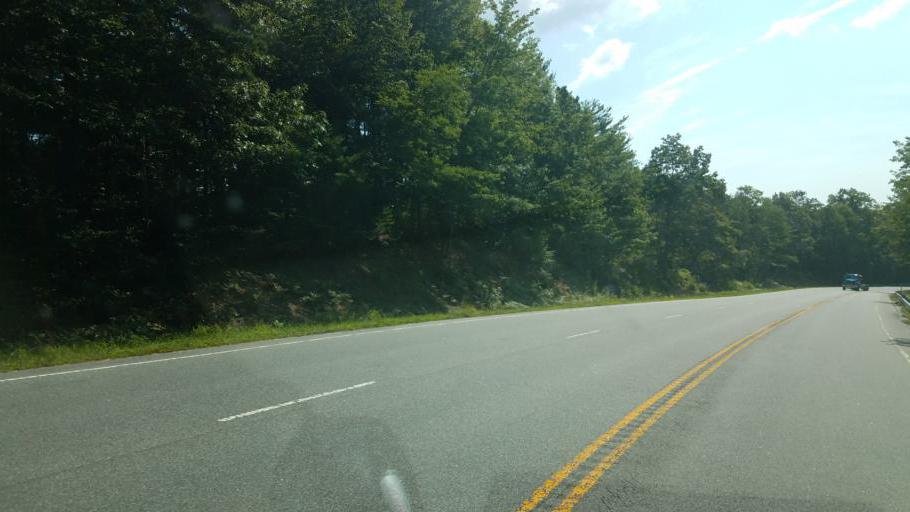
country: US
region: North Carolina
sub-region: Avery County
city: Newland
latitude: 35.9353
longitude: -81.8297
